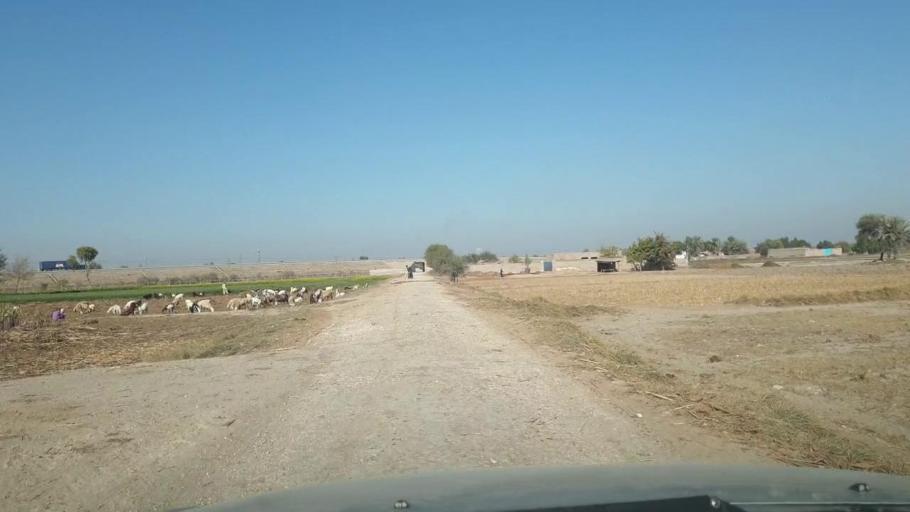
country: PK
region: Sindh
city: Ghotki
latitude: 28.0506
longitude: 69.3376
